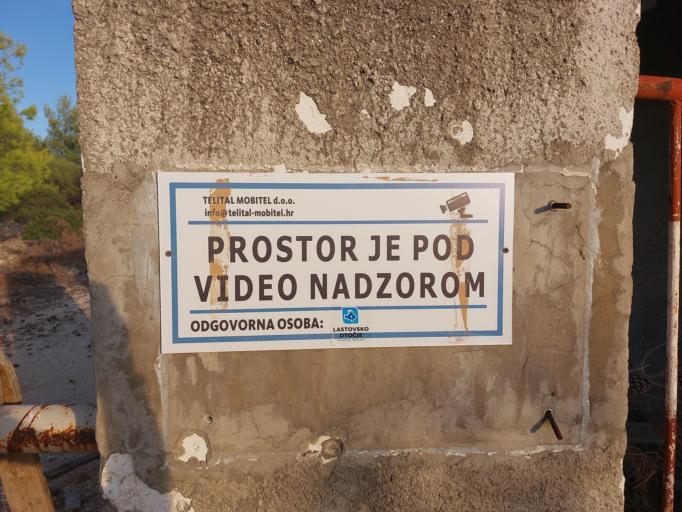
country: HR
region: Dubrovacko-Neretvanska
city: Smokvica
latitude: 42.7328
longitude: 16.8379
